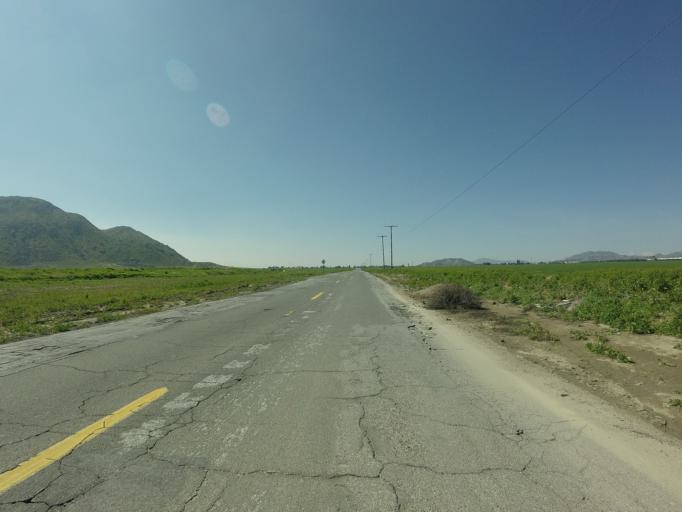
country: US
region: California
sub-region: Riverside County
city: Lakeview
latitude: 33.9194
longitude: -117.1270
